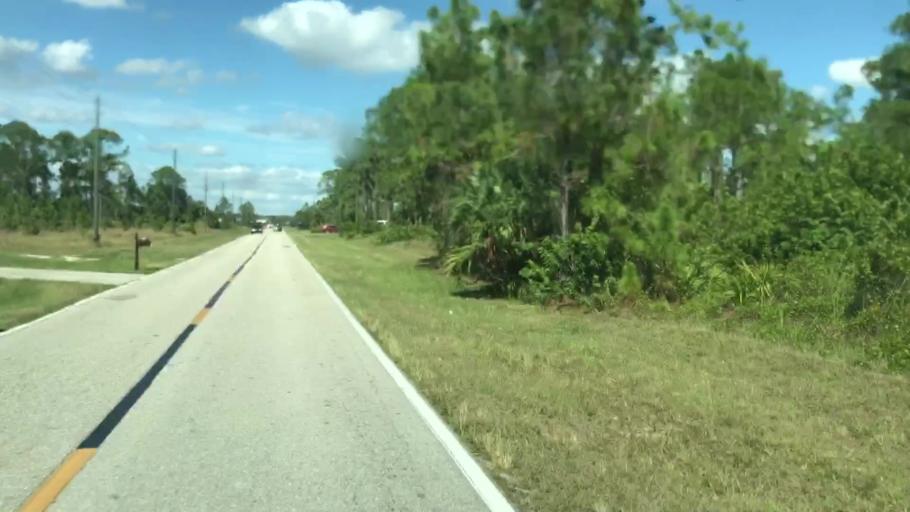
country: US
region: Florida
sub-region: Lee County
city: Lehigh Acres
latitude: 26.6663
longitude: -81.6257
